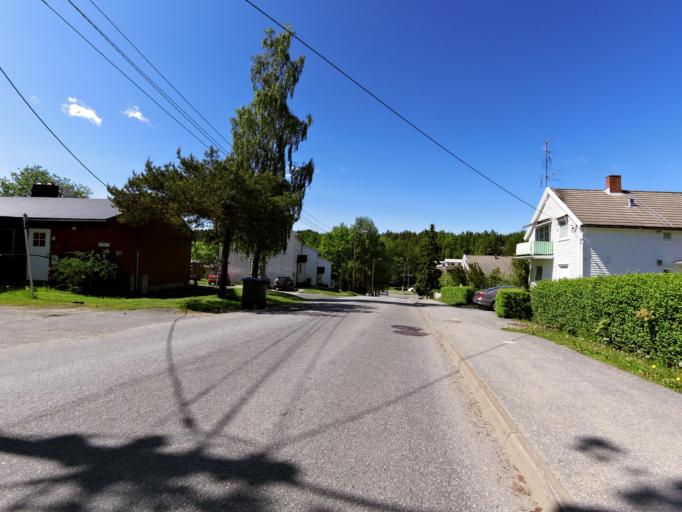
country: NO
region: Ostfold
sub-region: Fredrikstad
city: Fredrikstad
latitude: 59.2317
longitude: 10.9635
